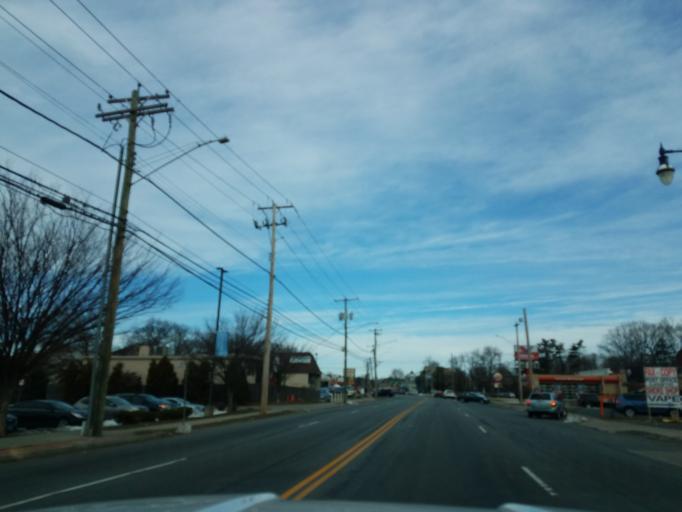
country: US
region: Connecticut
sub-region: Fairfield County
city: Trumbull
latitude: 41.2162
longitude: -73.2133
